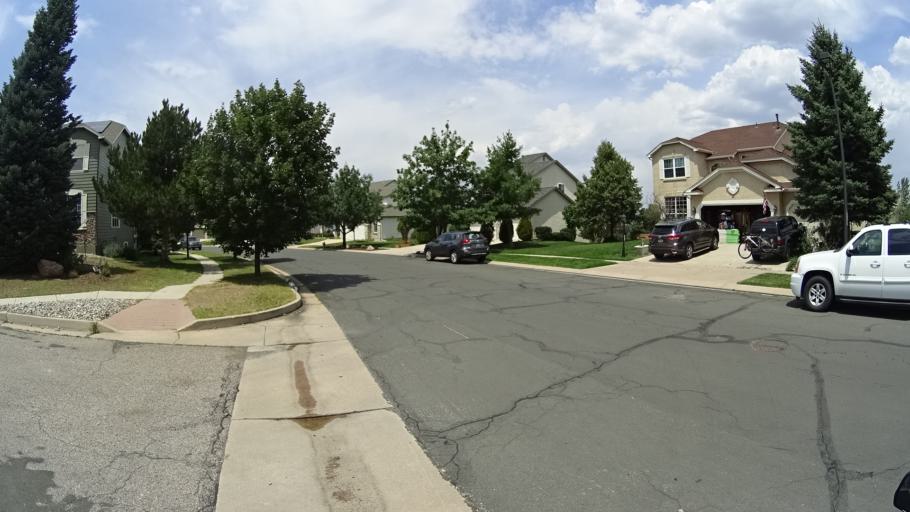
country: US
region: Colorado
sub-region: El Paso County
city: Black Forest
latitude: 38.9658
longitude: -104.7727
